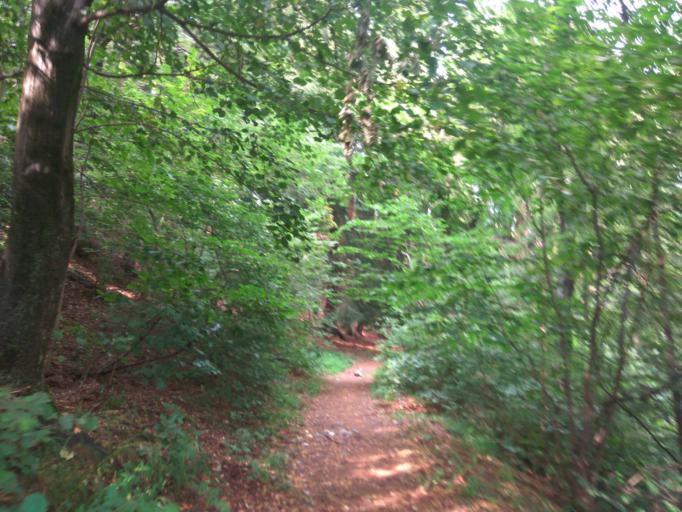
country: IT
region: Lombardy
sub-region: Provincia di Como
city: Lanzo d'Intelvi
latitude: 45.9878
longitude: 9.0280
